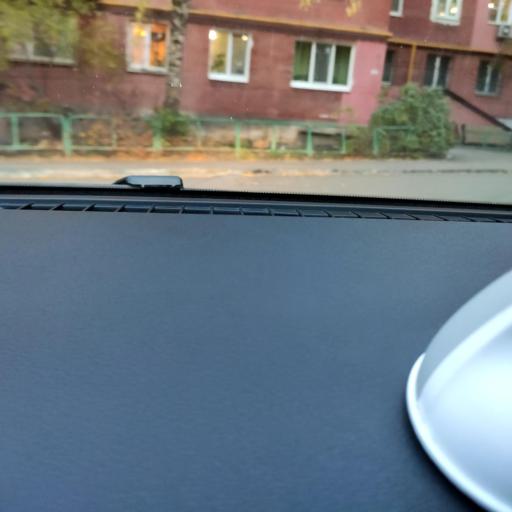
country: RU
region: Samara
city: Samara
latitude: 53.2144
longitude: 50.1330
